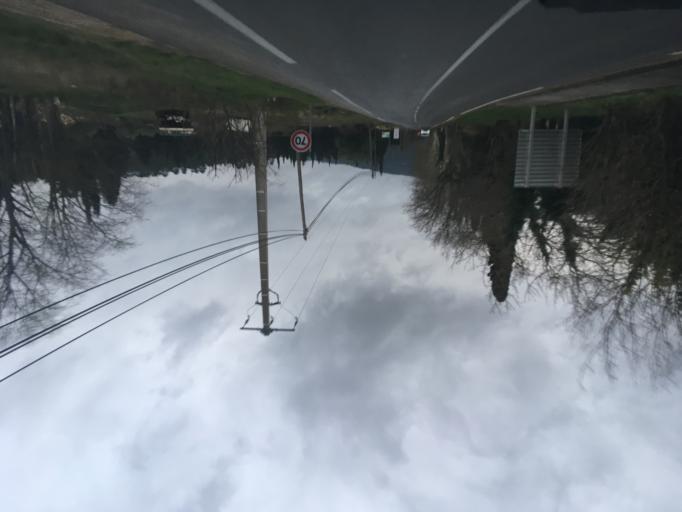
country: FR
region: Provence-Alpes-Cote d'Azur
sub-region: Departement du Var
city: Besse-sur-Issole
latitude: 43.3446
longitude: 6.1720
